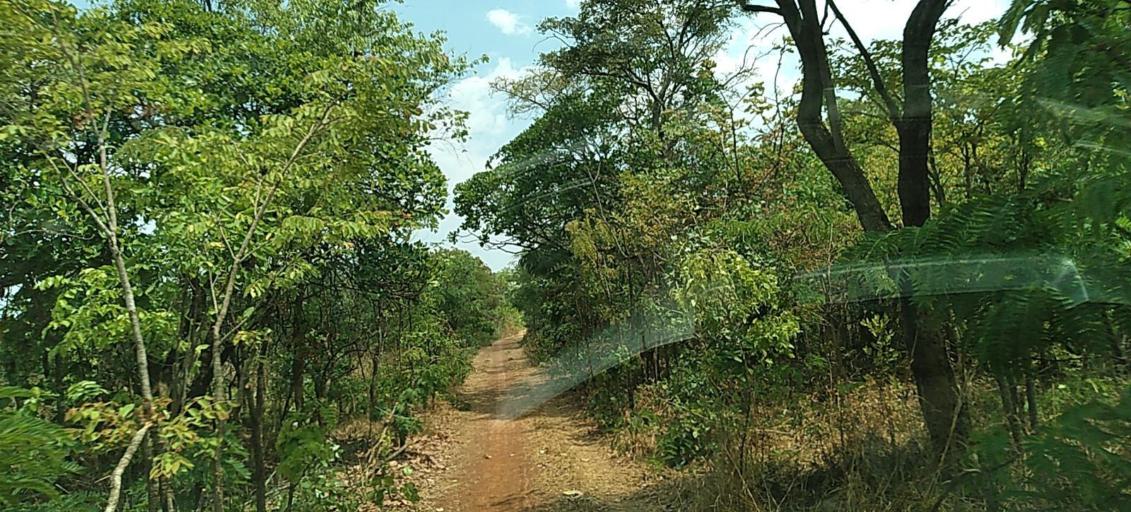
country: CD
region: Katanga
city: Kipushi
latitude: -11.9838
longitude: 27.4158
